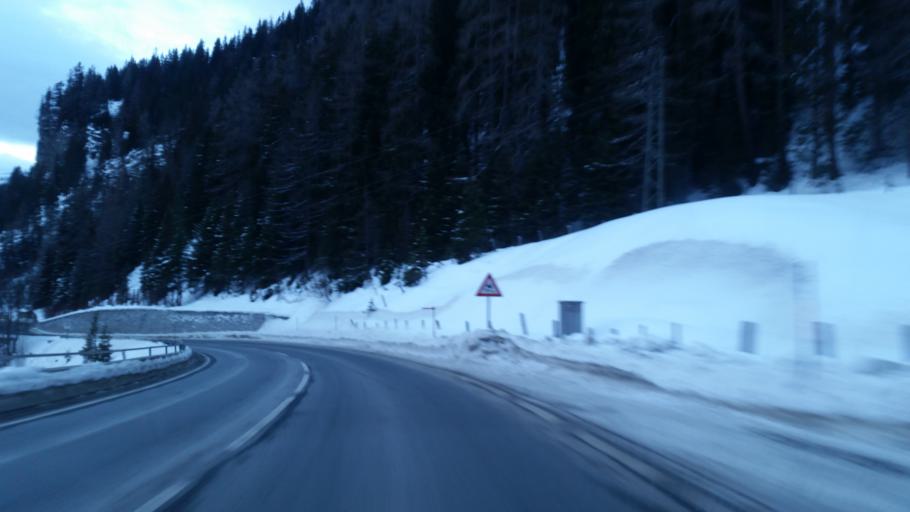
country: AT
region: Salzburg
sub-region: Politischer Bezirk Sankt Johann im Pongau
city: Untertauern
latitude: 47.2525
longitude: 13.5087
